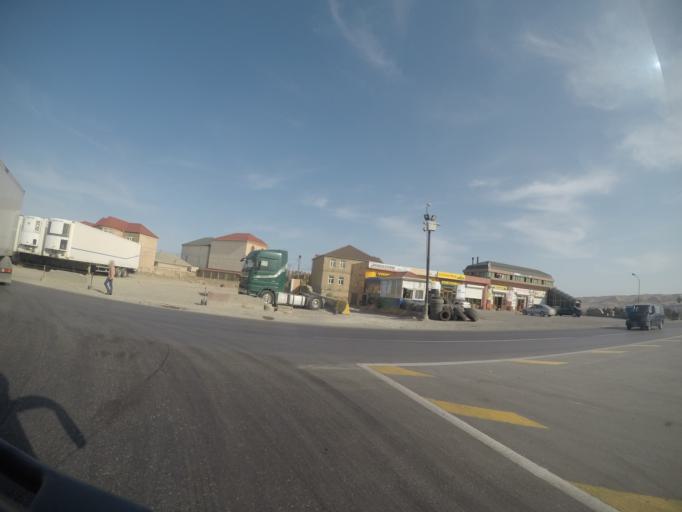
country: AZ
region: Abseron
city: Khirdalan
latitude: 40.4381
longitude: 49.7793
